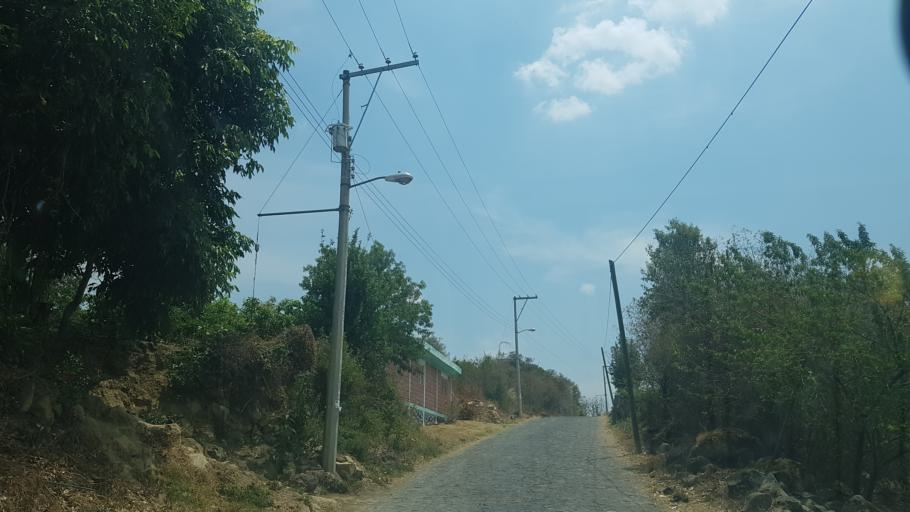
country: MX
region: Puebla
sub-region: Tochimilco
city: La Magdalena Yancuitlalpan
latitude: 18.8875
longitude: -98.6055
